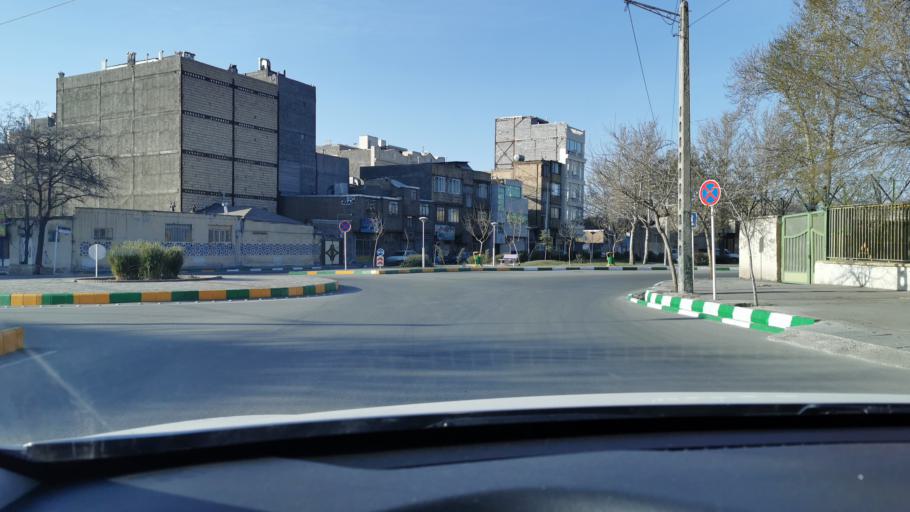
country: IR
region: Razavi Khorasan
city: Mashhad
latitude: 36.3020
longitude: 59.6332
